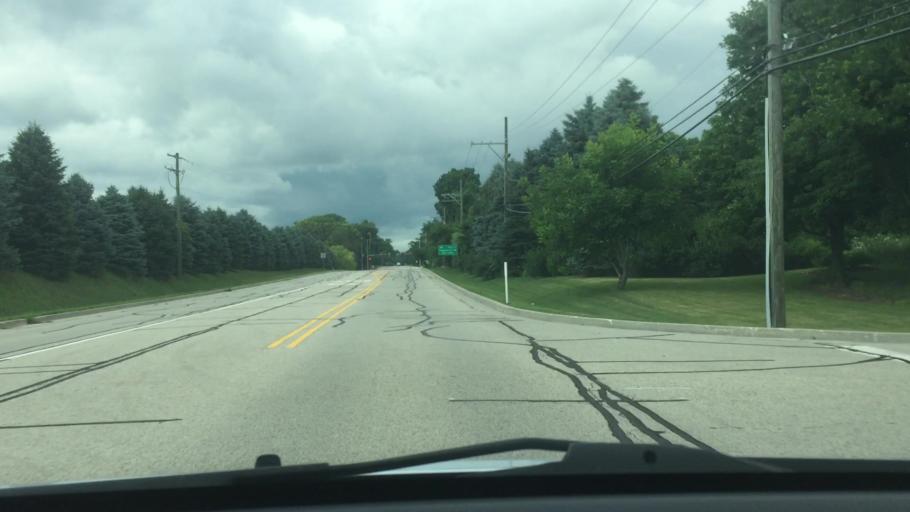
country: US
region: Illinois
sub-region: McHenry County
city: Crystal Lake
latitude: 42.2809
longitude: -88.3209
